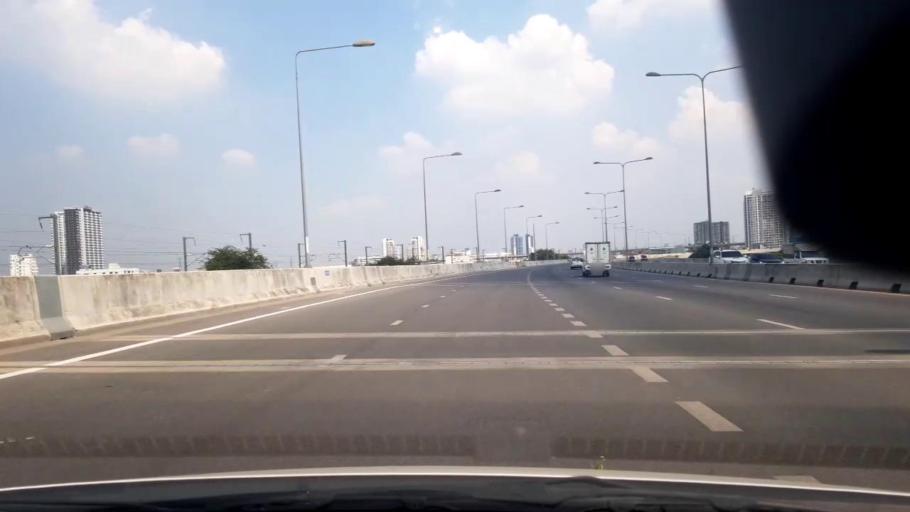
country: TH
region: Bangkok
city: Bang Sue
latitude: 13.8206
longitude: 100.5236
